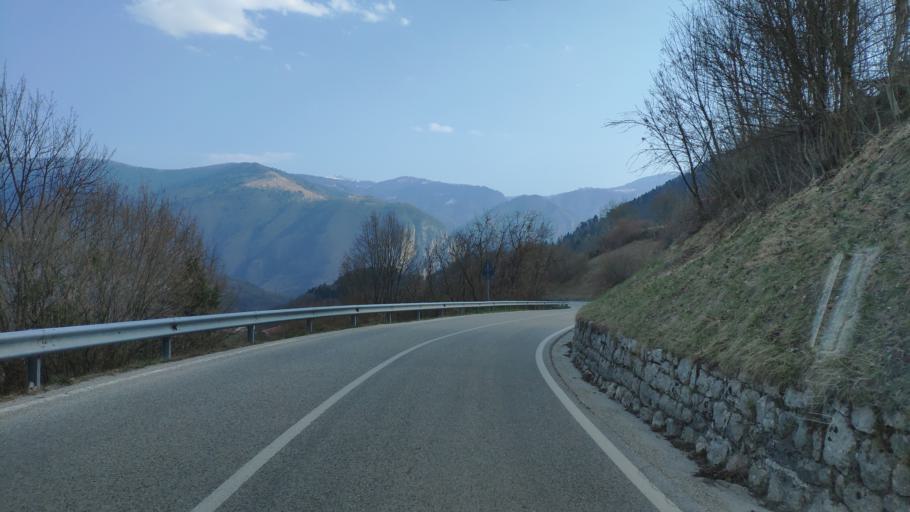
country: IT
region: Veneto
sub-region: Provincia di Vicenza
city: Enego
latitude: 45.9462
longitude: 11.7125
